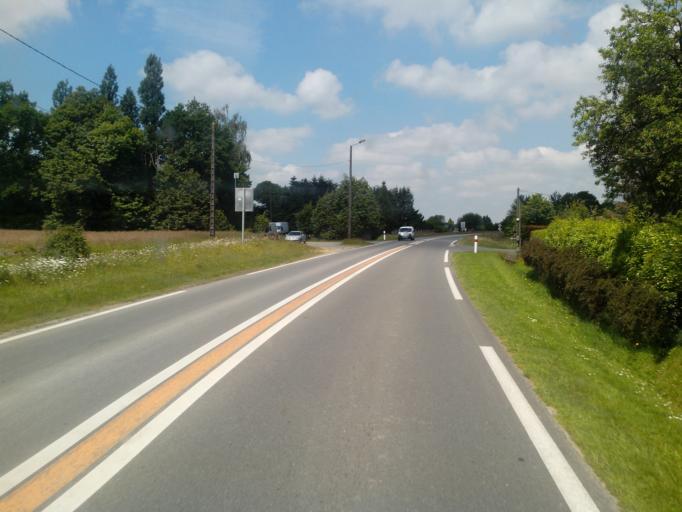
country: FR
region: Brittany
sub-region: Departement d'Ille-et-Vilaine
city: Lecousse
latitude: 48.3728
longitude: -1.2452
